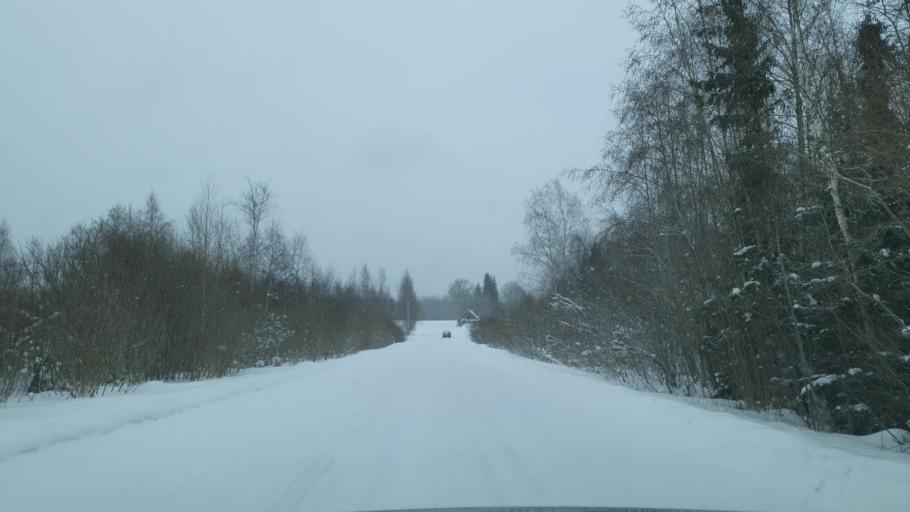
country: EE
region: Tartu
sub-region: Tartu linn
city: Tartu
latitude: 58.5748
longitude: 26.8147
